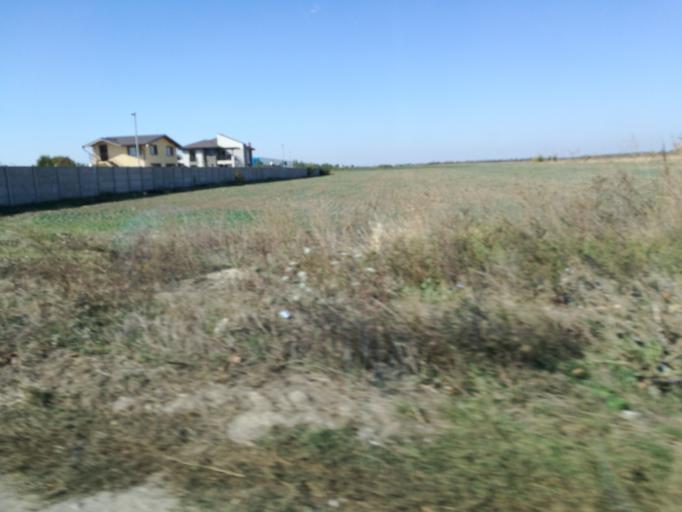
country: RO
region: Giurgiu
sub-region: Comuna Joita
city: Bacu
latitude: 44.4678
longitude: 25.8840
